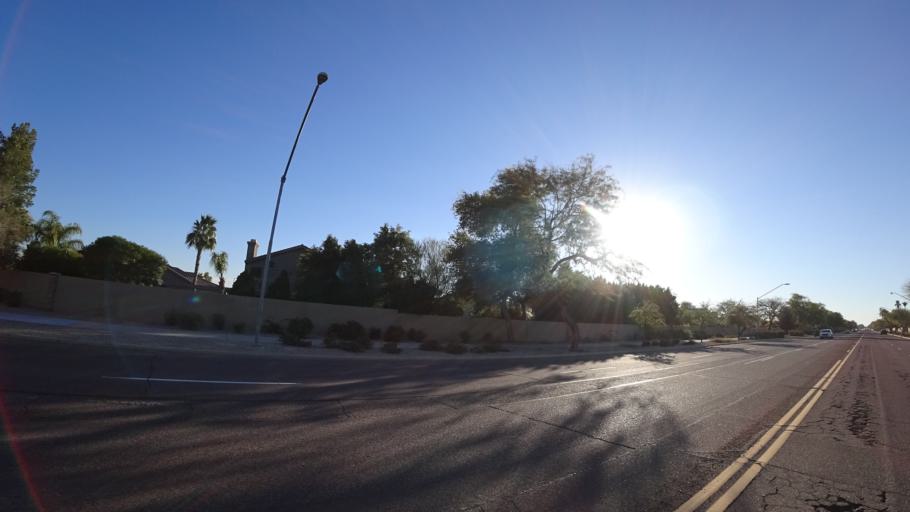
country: US
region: Arizona
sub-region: Maricopa County
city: Sun City
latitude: 33.6818
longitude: -112.2122
